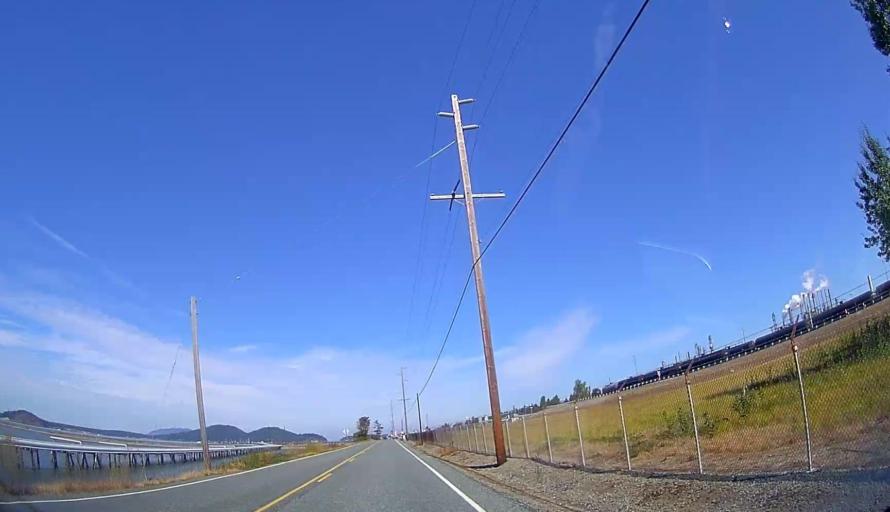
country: US
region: Washington
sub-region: Skagit County
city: Anacortes
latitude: 48.4889
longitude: -122.5757
